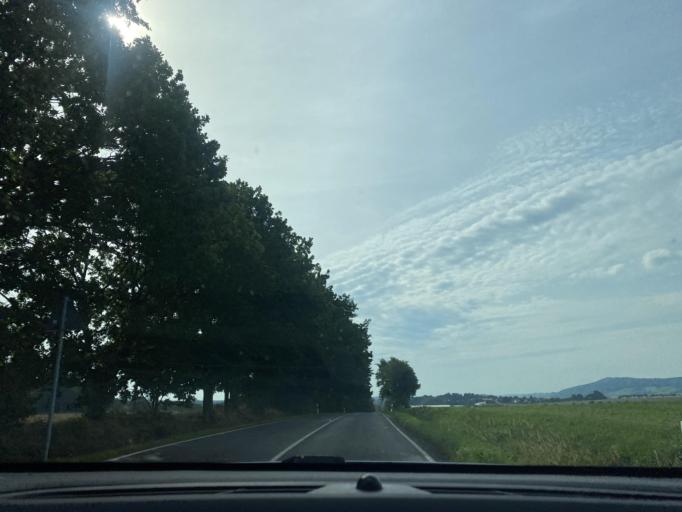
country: DE
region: Saxony
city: Reichenbach
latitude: 51.1576
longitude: 14.7956
